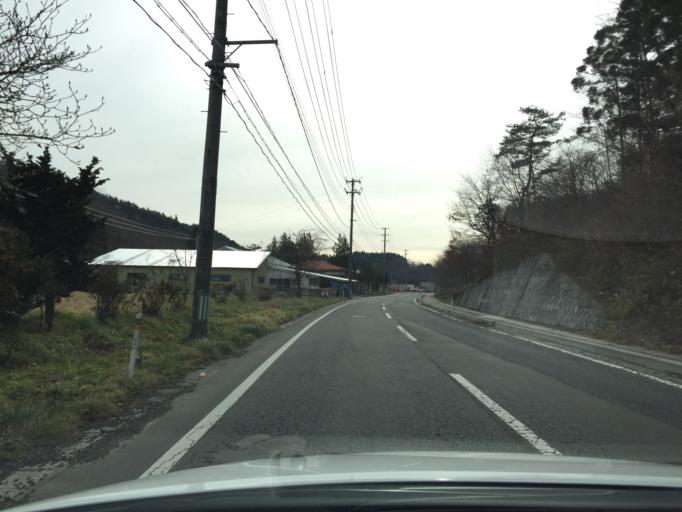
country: JP
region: Fukushima
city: Ishikawa
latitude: 37.2283
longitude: 140.5674
